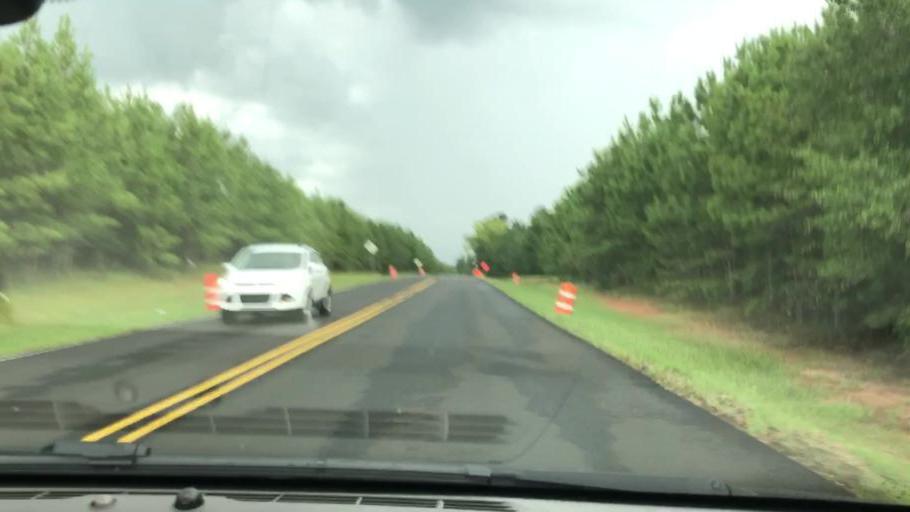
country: US
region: Georgia
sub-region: Clay County
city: Fort Gaines
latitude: 31.5116
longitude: -85.0213
